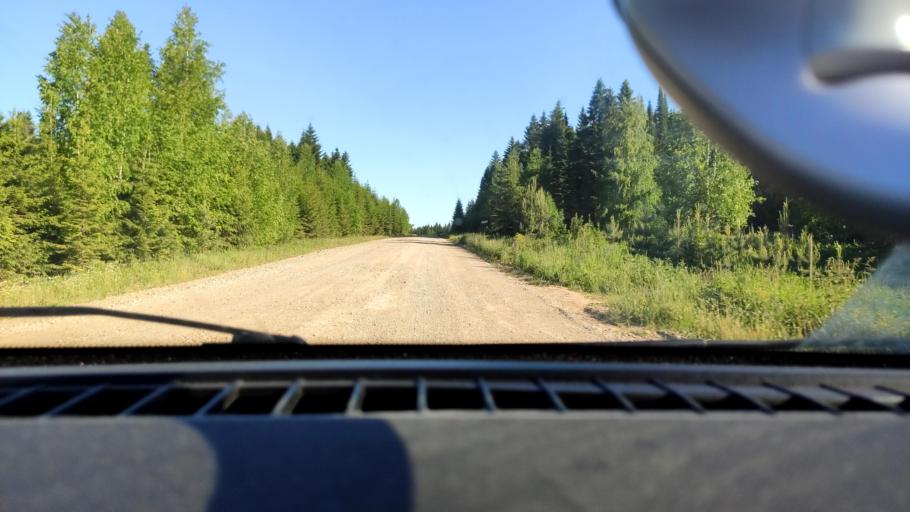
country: RU
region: Perm
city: Novyye Lyady
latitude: 58.1759
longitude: 56.5929
